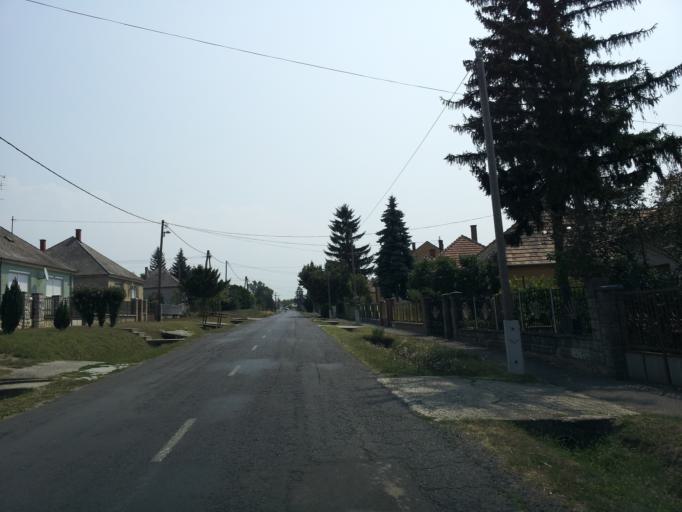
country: HU
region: Gyor-Moson-Sopron
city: Pannonhalma
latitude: 47.5054
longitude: 17.7848
